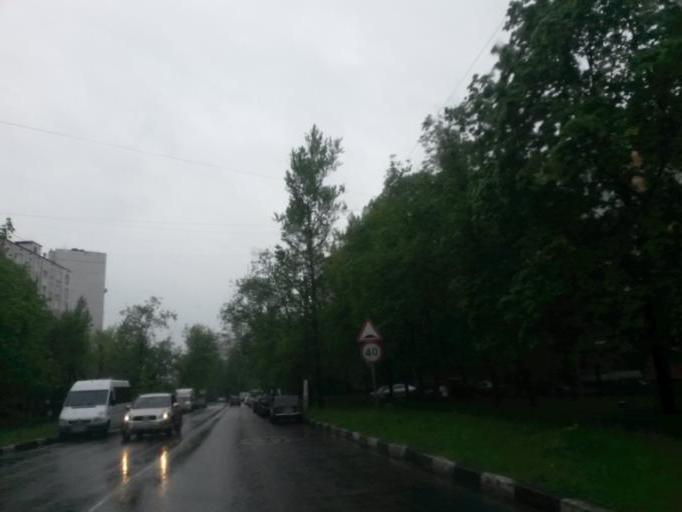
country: RU
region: Moscow
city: Zyablikovo
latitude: 55.6184
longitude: 37.7536
